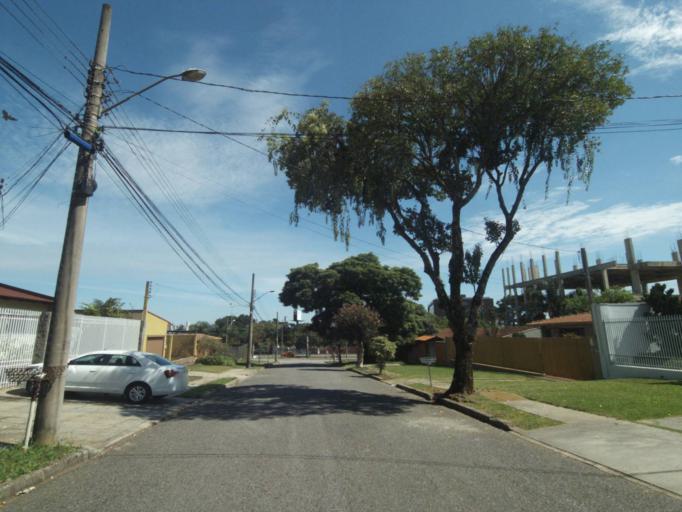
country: BR
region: Parana
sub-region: Curitiba
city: Curitiba
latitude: -25.4550
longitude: -49.2457
